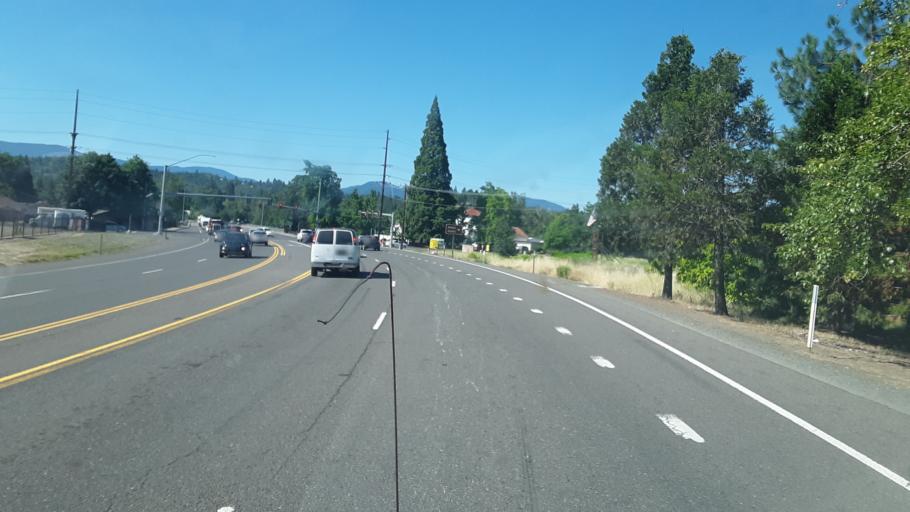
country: US
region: Oregon
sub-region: Josephine County
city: Fruitdale
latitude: 42.4322
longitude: -123.3176
